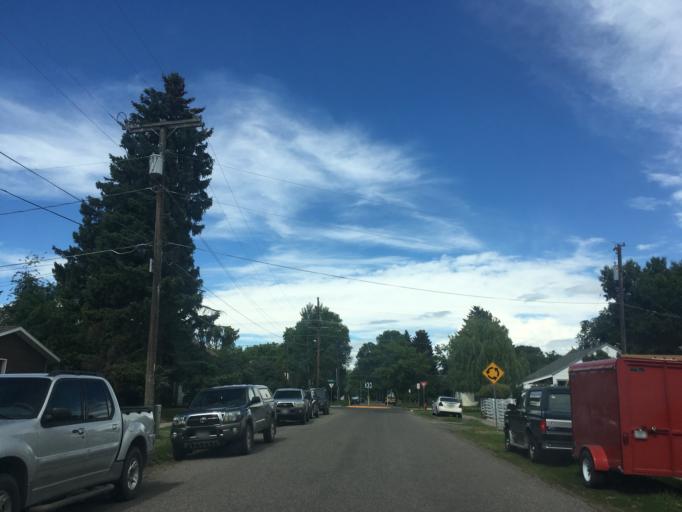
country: US
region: Montana
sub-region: Gallatin County
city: Bozeman
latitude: 45.6838
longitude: -111.0274
